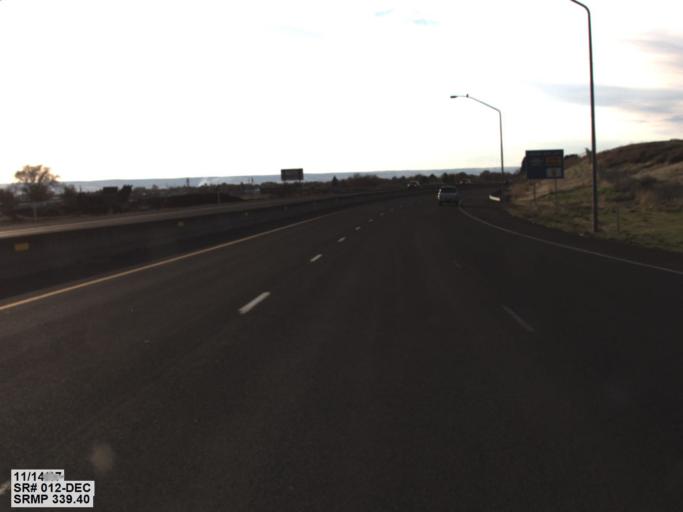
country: US
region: Washington
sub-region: Walla Walla County
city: Walla Walla East
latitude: 46.0829
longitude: -118.2901
